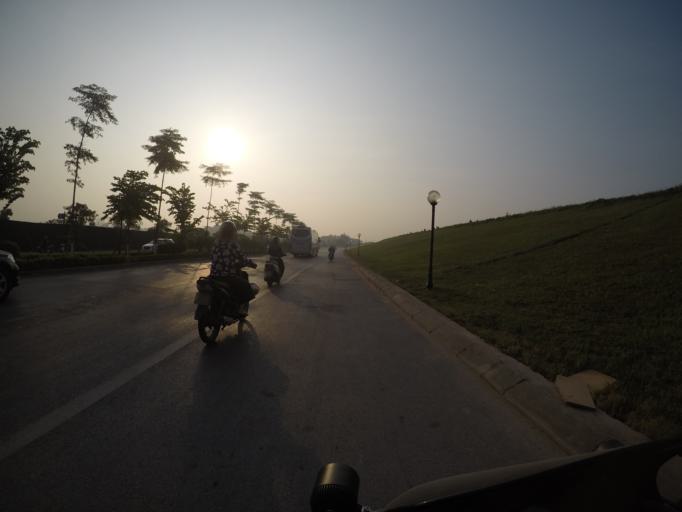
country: VN
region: Ha Noi
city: Hoan Kiem
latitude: 21.0311
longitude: 105.8797
